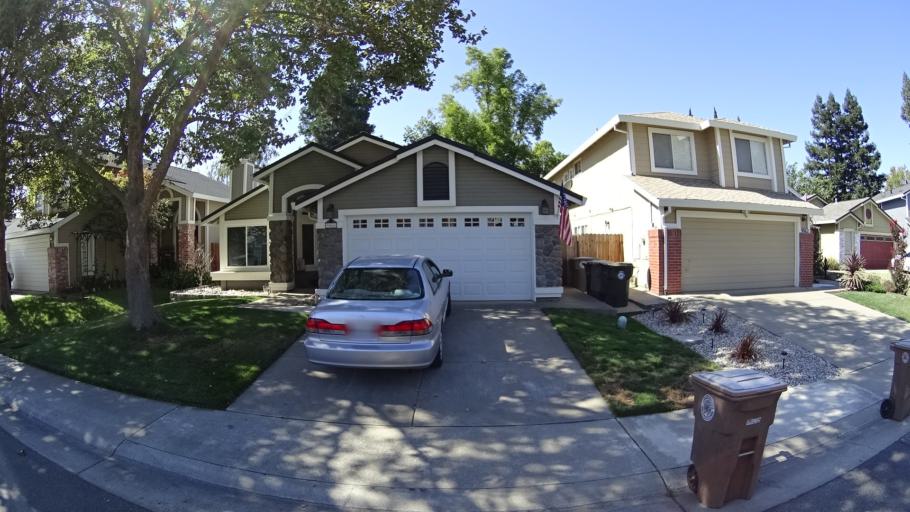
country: US
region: California
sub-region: Sacramento County
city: Laguna
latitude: 38.4284
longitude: -121.4255
